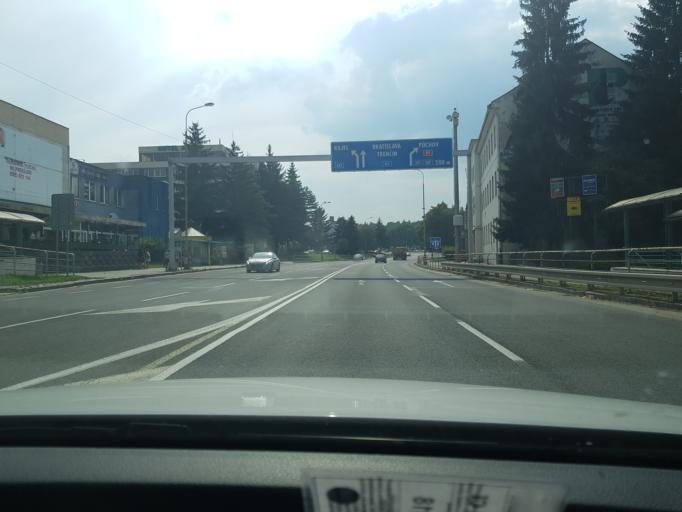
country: SK
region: Trenciansky
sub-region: Okres Povazska Bystrica
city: Povazska Bystrica
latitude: 49.1170
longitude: 18.4461
